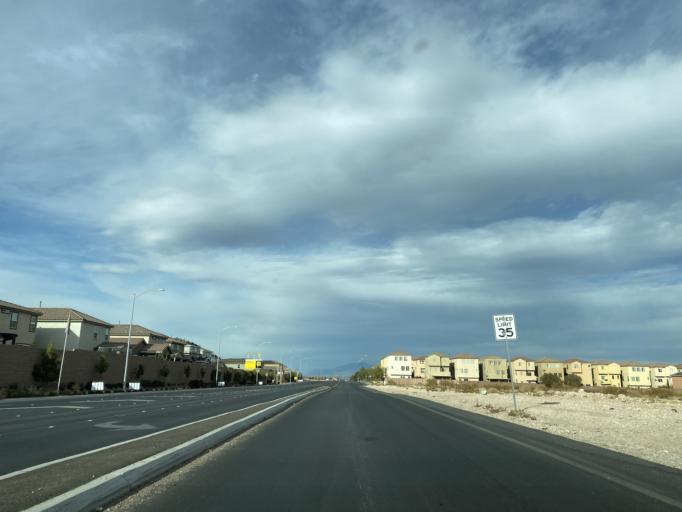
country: US
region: Nevada
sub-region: Clark County
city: Enterprise
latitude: 36.0123
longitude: -115.2982
